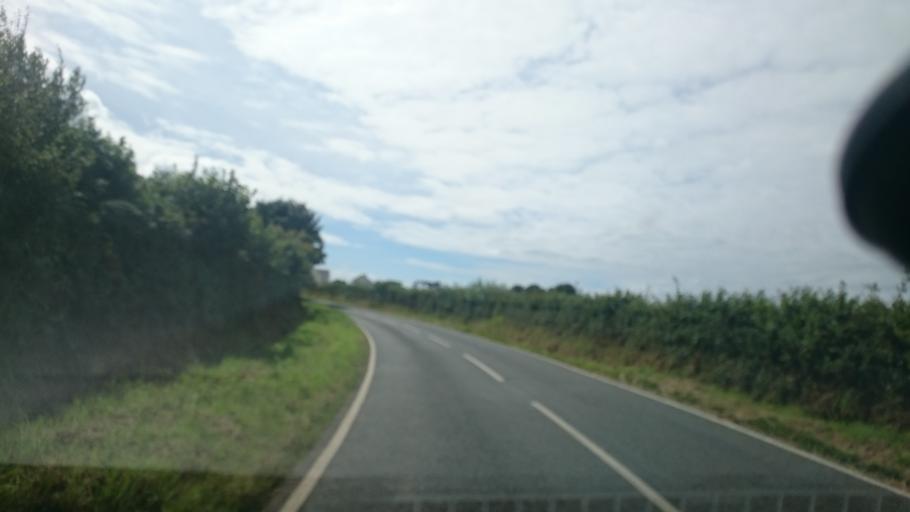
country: GB
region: Wales
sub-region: Pembrokeshire
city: Freystrop
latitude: 51.7524
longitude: -4.9501
